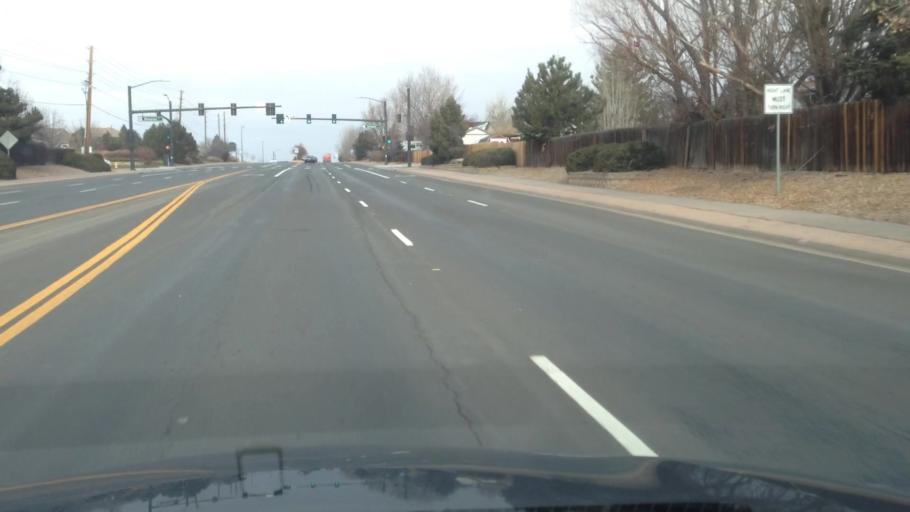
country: US
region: Colorado
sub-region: Arapahoe County
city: Dove Valley
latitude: 39.5641
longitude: -104.7997
